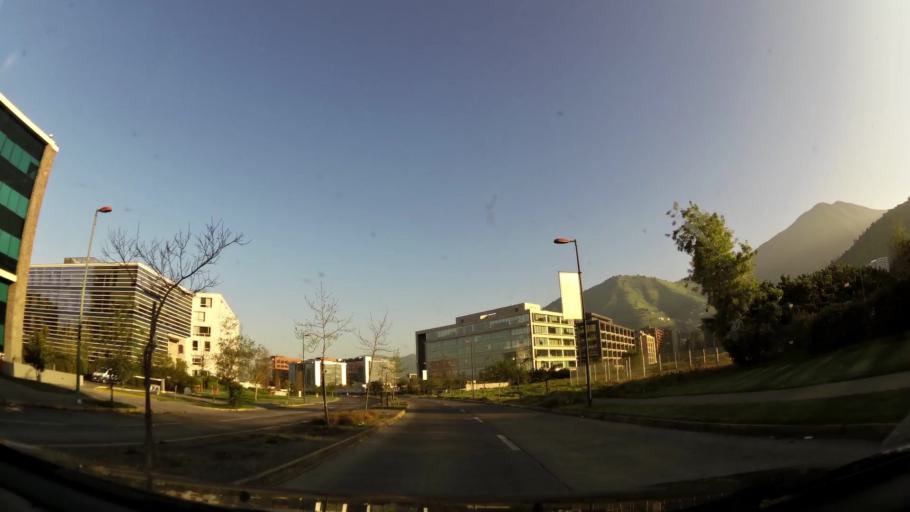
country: CL
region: Santiago Metropolitan
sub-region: Provincia de Santiago
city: Santiago
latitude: -33.3893
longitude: -70.6139
